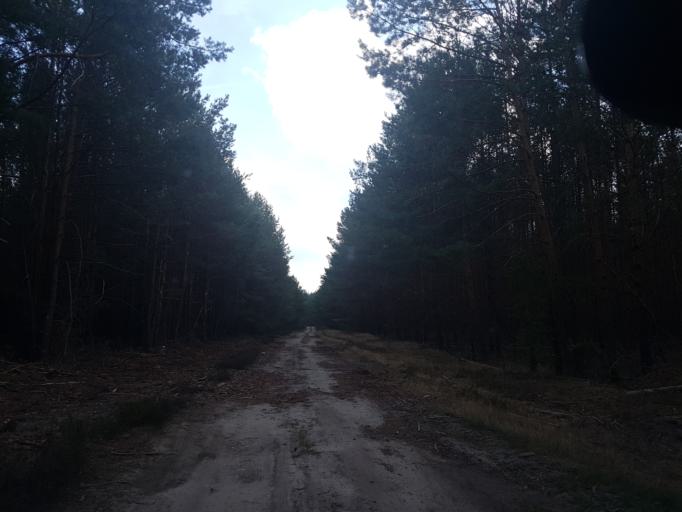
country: DE
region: Brandenburg
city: Treuenbrietzen
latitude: 52.0497
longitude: 12.8473
